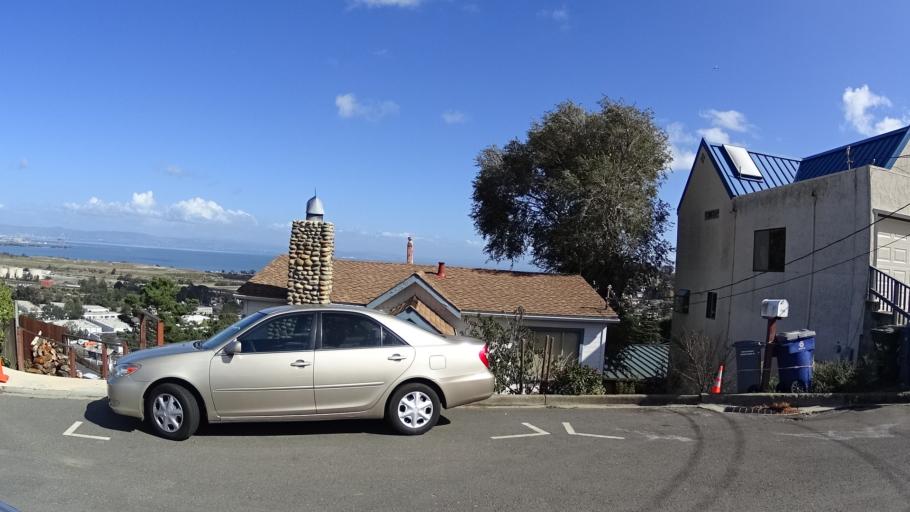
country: US
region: California
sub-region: San Mateo County
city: Brisbane
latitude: 37.6845
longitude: -122.4080
